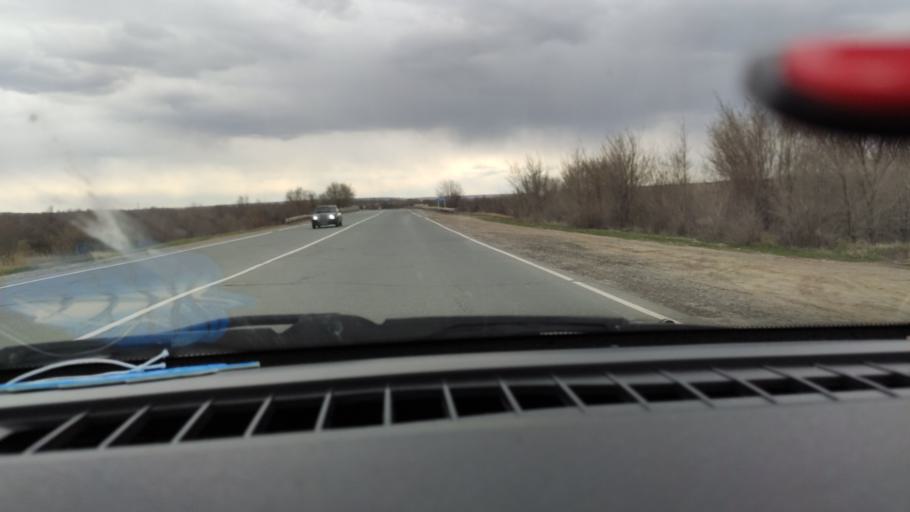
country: RU
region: Saratov
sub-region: Saratovskiy Rayon
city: Saratov
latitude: 51.7216
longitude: 46.0266
